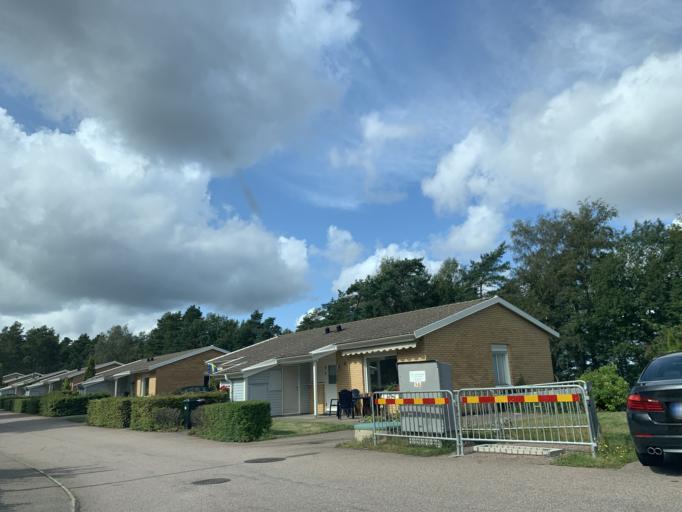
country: SE
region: Vaestra Goetaland
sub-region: Goteborg
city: Eriksbo
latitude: 57.7667
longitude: 12.0468
